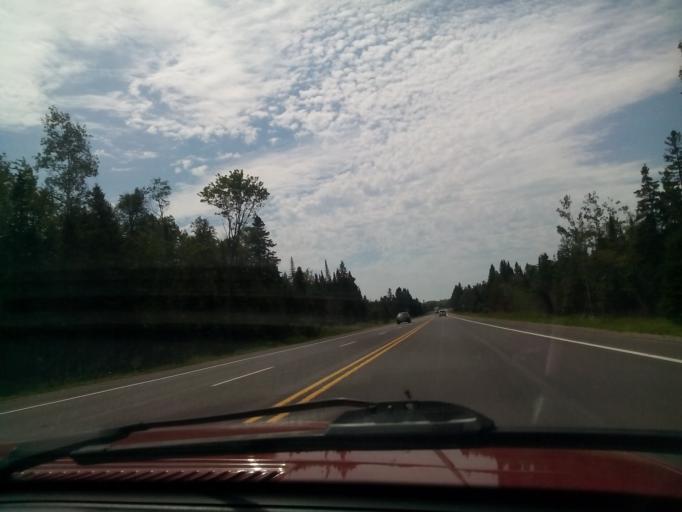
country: US
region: Michigan
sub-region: Schoolcraft County
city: Manistique
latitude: 46.0043
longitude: -85.9999
